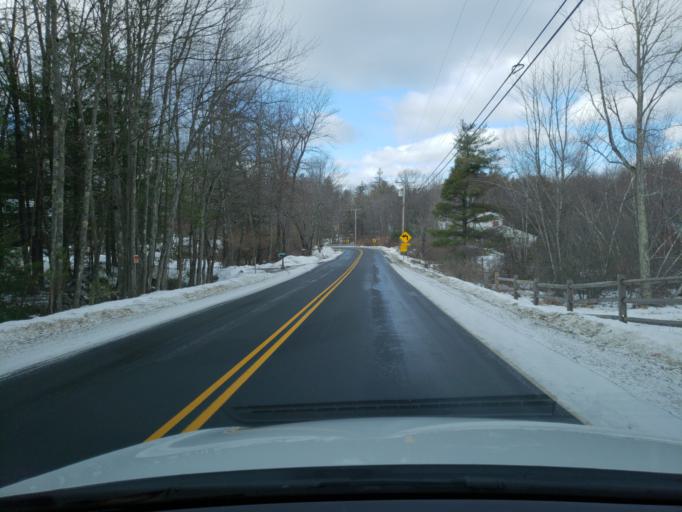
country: US
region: New Hampshire
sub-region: Hillsborough County
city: Deering
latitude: 43.0137
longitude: -71.8604
